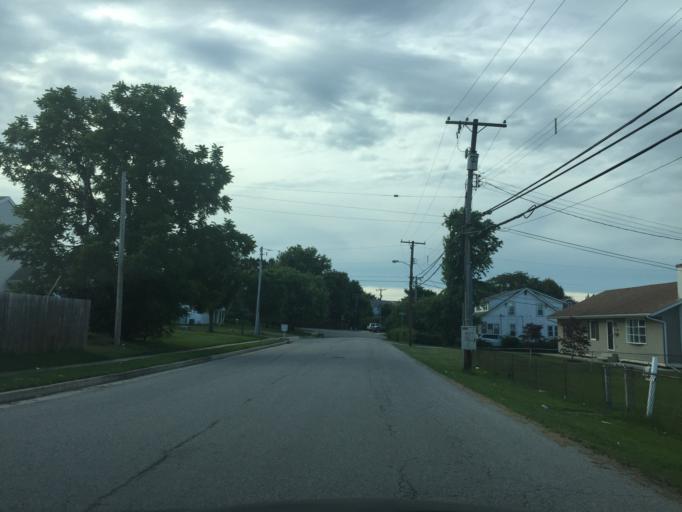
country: US
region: Maryland
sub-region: Baltimore County
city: Middle River
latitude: 39.3384
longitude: -76.4447
